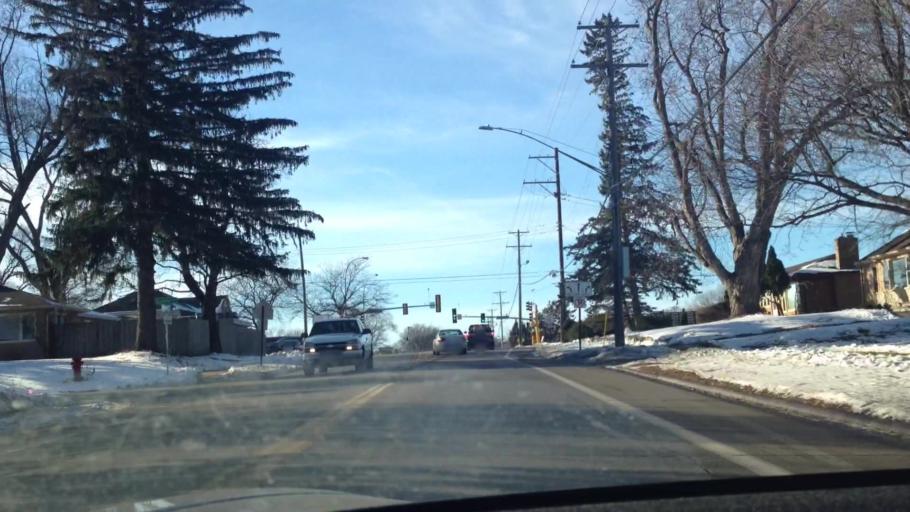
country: US
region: Minnesota
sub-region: Hennepin County
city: Saint Louis Park
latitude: 44.9495
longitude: -93.3793
